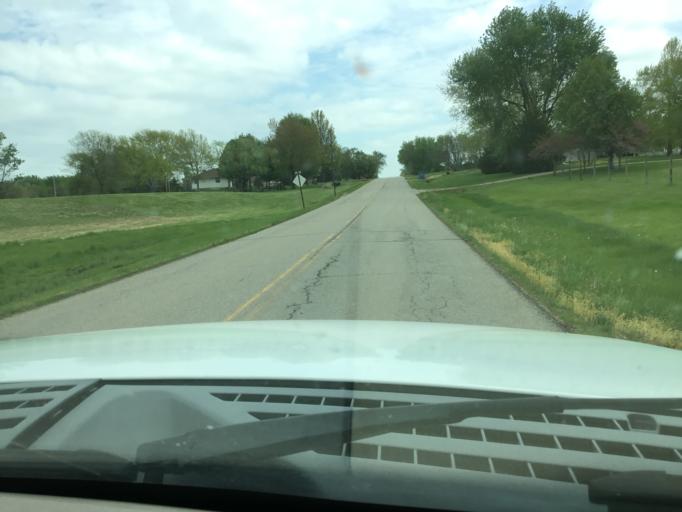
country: US
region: Kansas
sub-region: Shawnee County
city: Auburn
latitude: 38.9709
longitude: -95.8153
